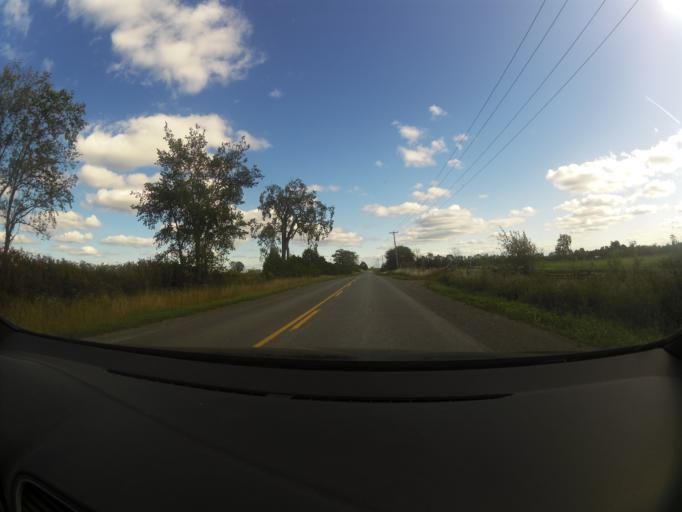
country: CA
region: Ontario
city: Carleton Place
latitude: 45.1833
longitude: -76.1123
